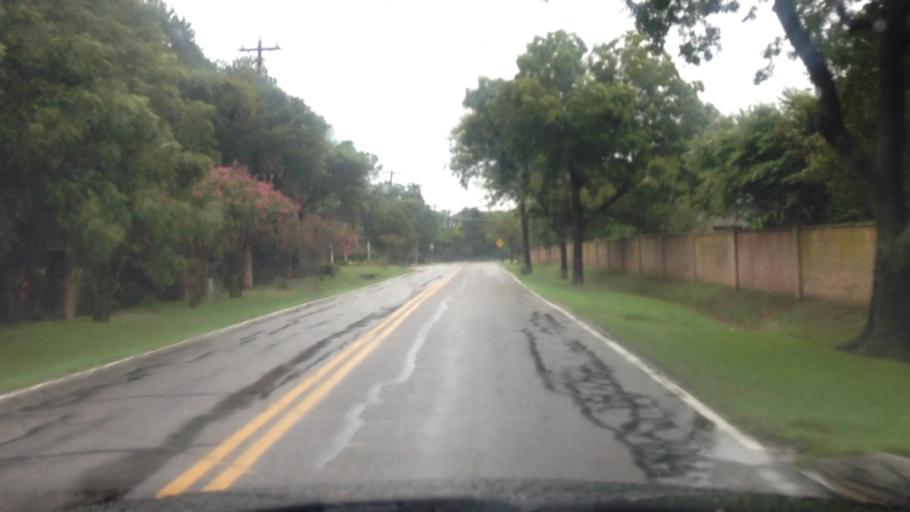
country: US
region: Texas
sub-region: Tarrant County
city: Keller
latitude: 32.9119
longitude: -97.2282
